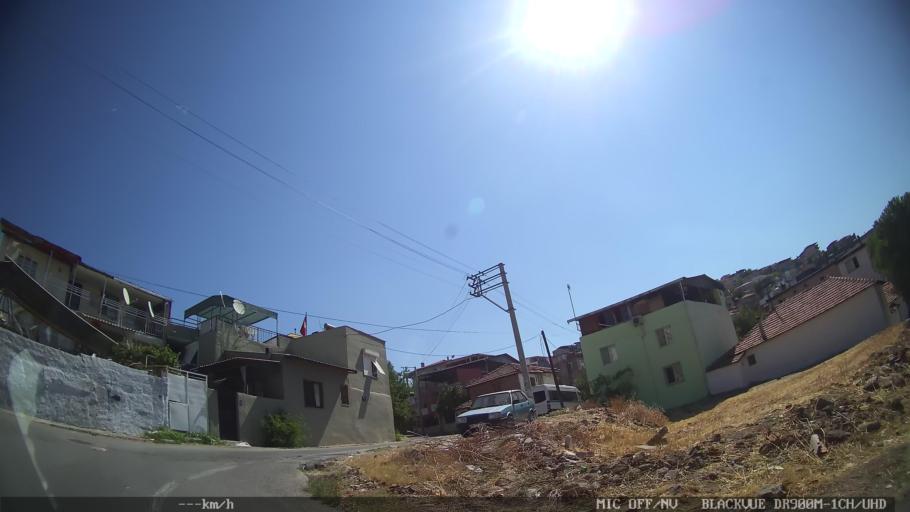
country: TR
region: Izmir
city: Karsiyaka
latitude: 38.5020
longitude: 27.0692
